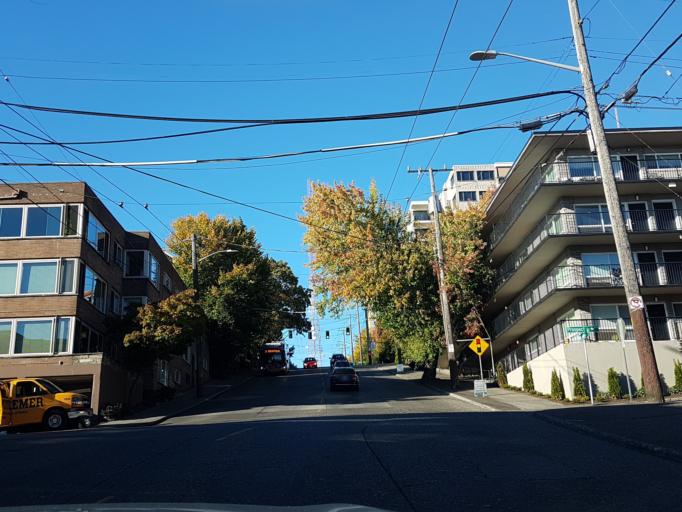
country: US
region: Washington
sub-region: King County
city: Seattle
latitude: 47.6285
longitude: -122.3566
